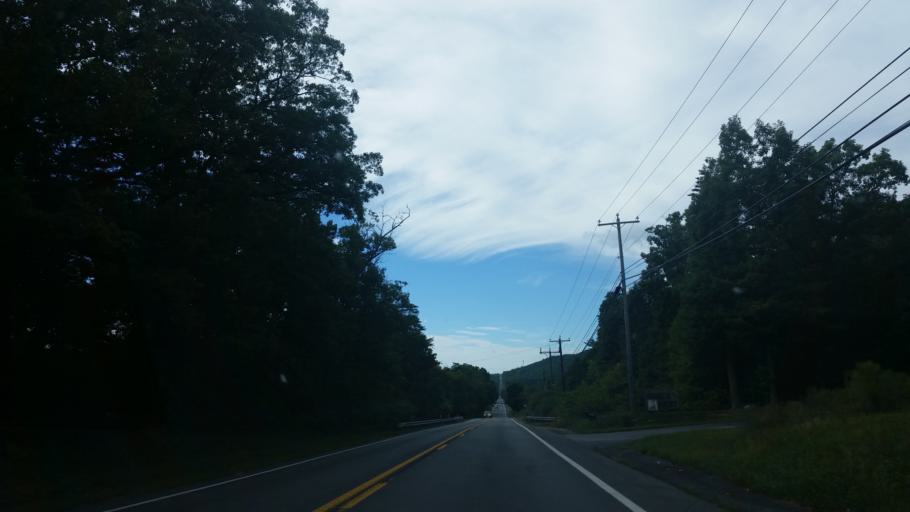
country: US
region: West Virginia
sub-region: Morgan County
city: Berkeley Springs
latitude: 39.5414
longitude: -78.2728
